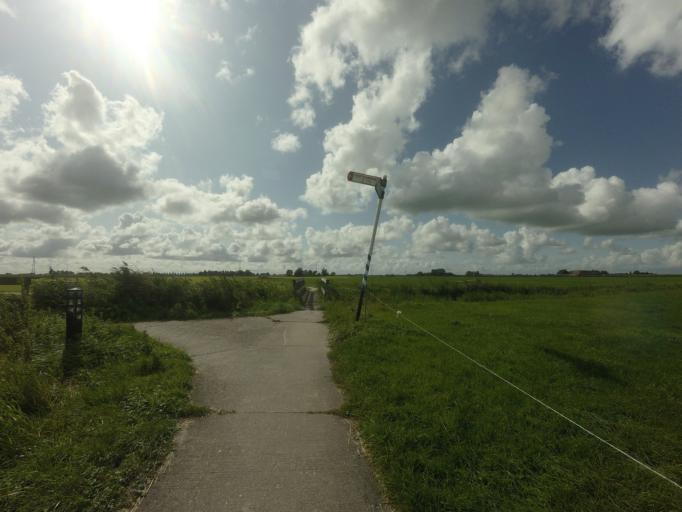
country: NL
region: Friesland
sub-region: Sudwest Fryslan
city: Sneek
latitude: 53.0670
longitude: 5.6395
